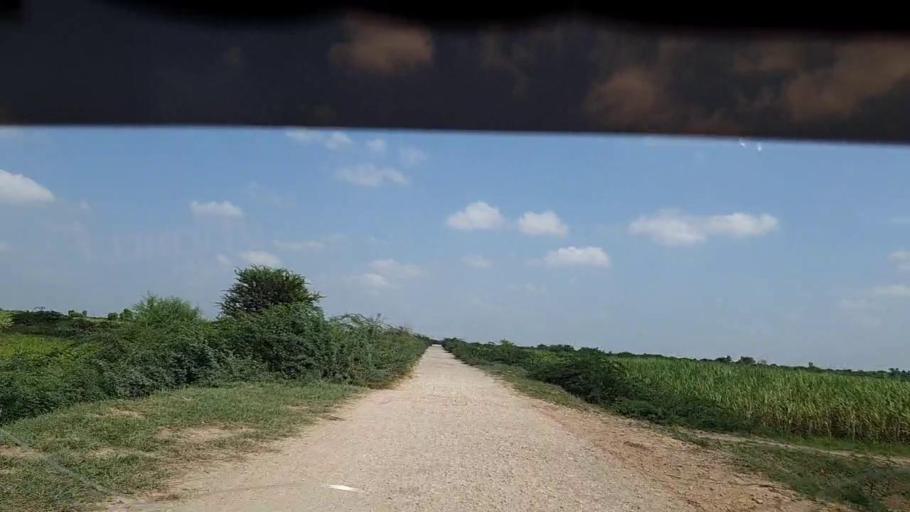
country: PK
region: Sindh
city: Kadhan
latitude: 24.6034
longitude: 68.9822
